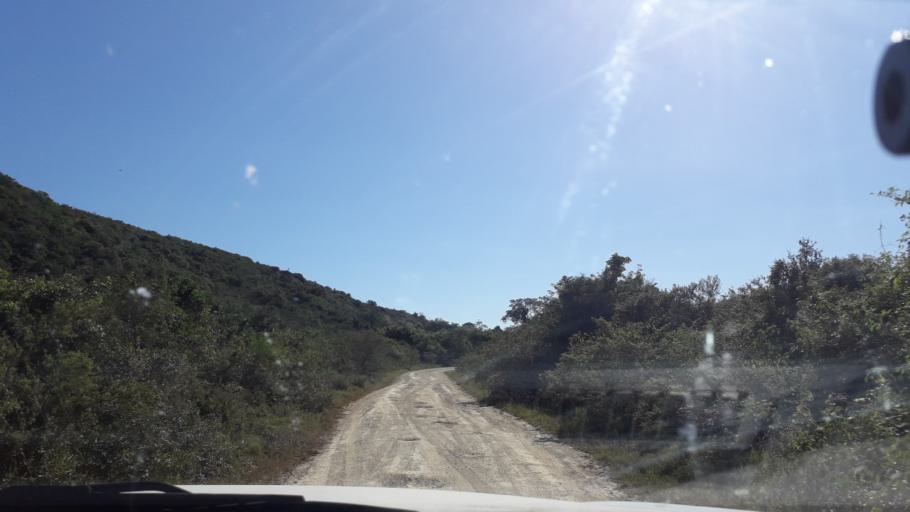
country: ZA
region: Eastern Cape
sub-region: Amathole District Municipality
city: Komga
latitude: -32.7673
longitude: 27.9624
